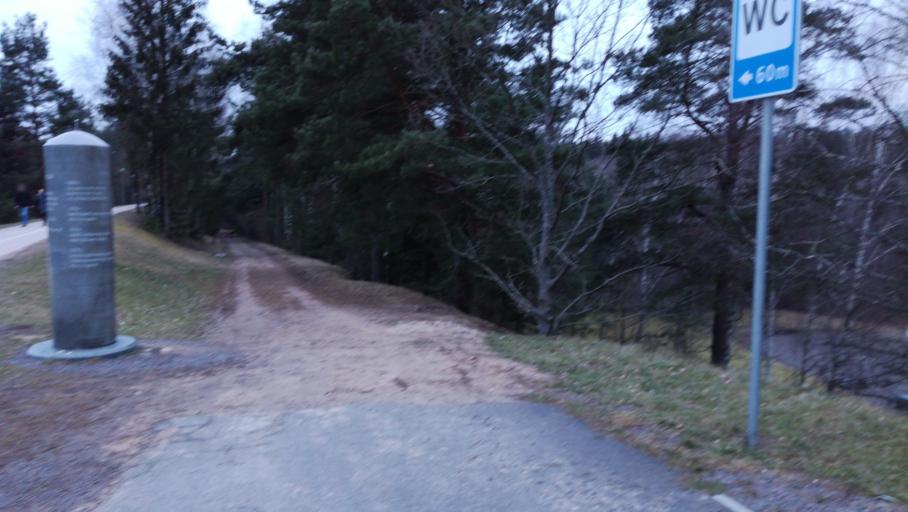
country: LT
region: Alytaus apskritis
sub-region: Alytus
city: Alytus
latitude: 54.3923
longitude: 24.0795
